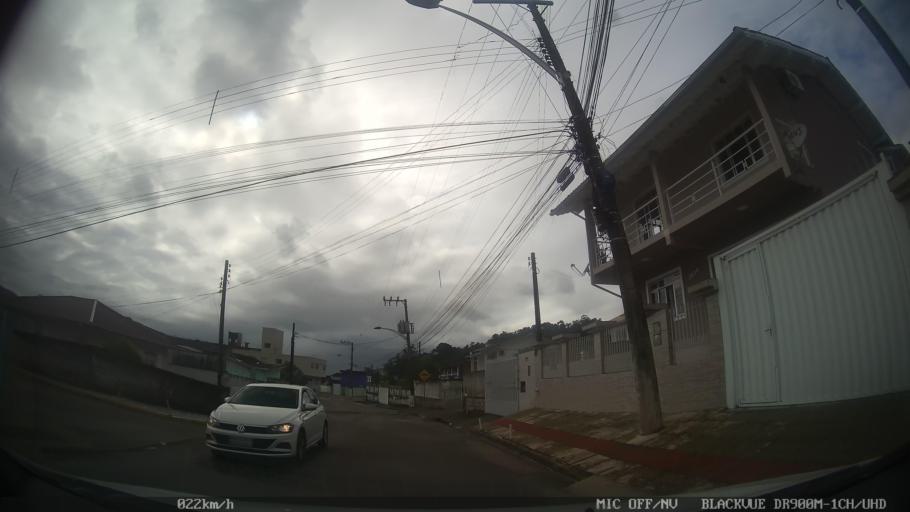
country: BR
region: Santa Catarina
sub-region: Biguacu
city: Biguacu
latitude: -27.5176
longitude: -48.6457
